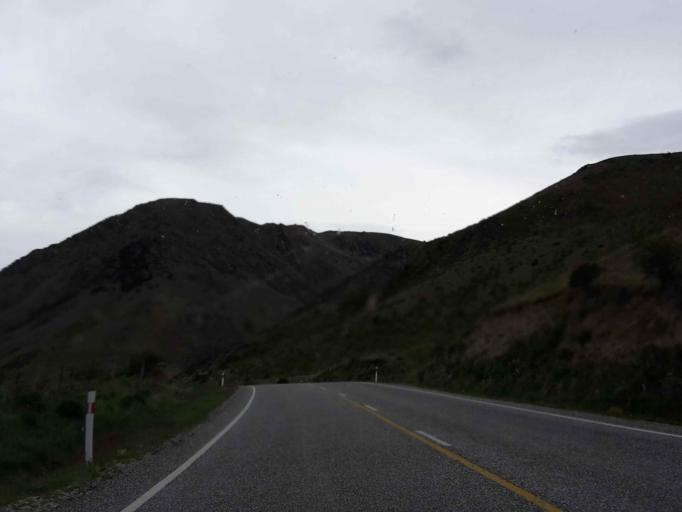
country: NZ
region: Otago
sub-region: Queenstown-Lakes District
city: Wanaka
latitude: -44.6108
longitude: 169.5334
